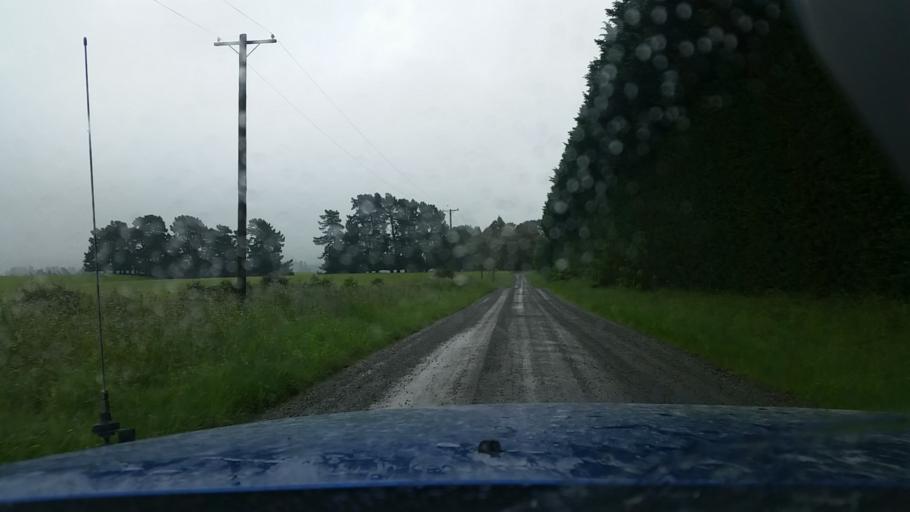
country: NZ
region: Canterbury
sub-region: Ashburton District
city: Methven
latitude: -43.7153
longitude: 171.3297
